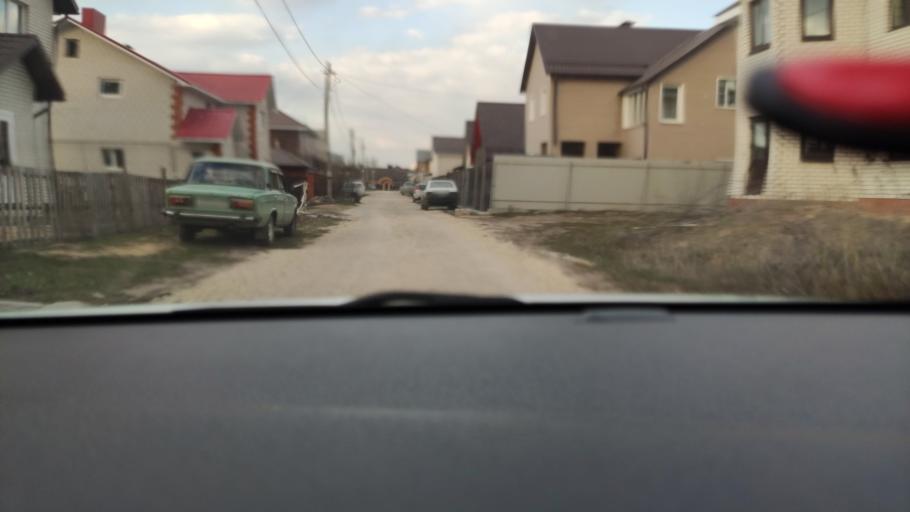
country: RU
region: Voronezj
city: Pridonskoy
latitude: 51.6337
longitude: 39.0967
